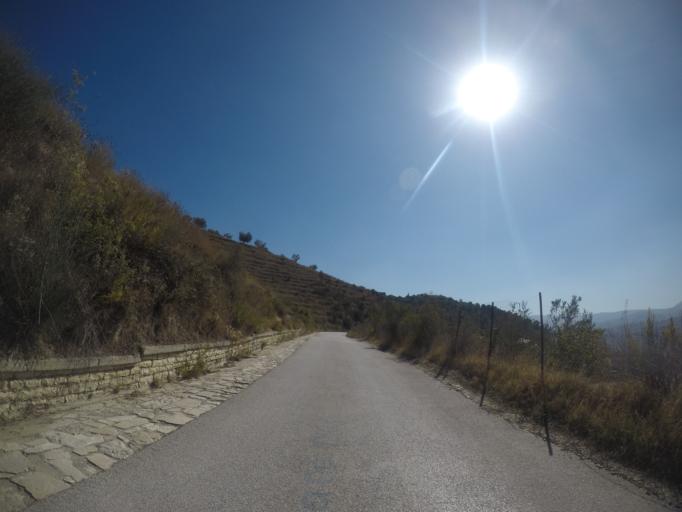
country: AL
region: Berat
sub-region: Rrethi i Beratit
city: Berat
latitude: 40.7146
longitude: 19.9444
